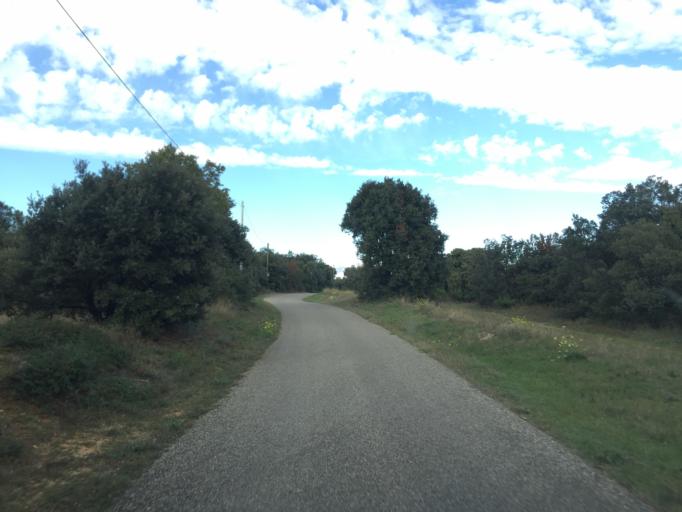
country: FR
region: Provence-Alpes-Cote d'Azur
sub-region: Departement du Vaucluse
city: Orange
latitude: 44.1067
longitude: 4.8126
